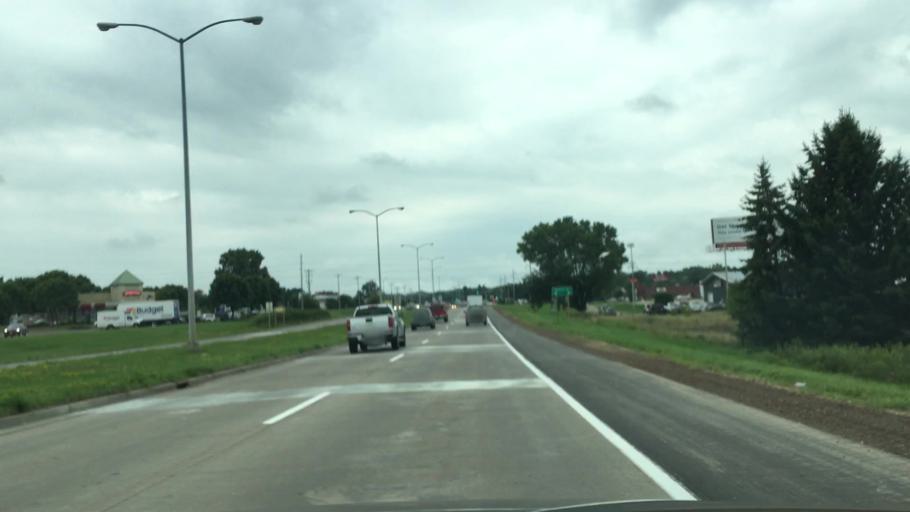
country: US
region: Wisconsin
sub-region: Eau Claire County
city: Eau Claire
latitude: 44.8270
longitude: -91.5443
